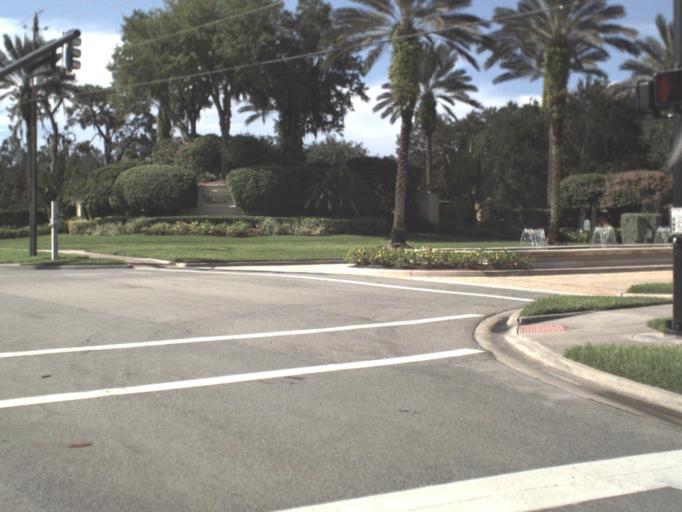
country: US
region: Florida
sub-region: Sarasota County
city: Vamo
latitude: 27.2149
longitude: -82.4904
